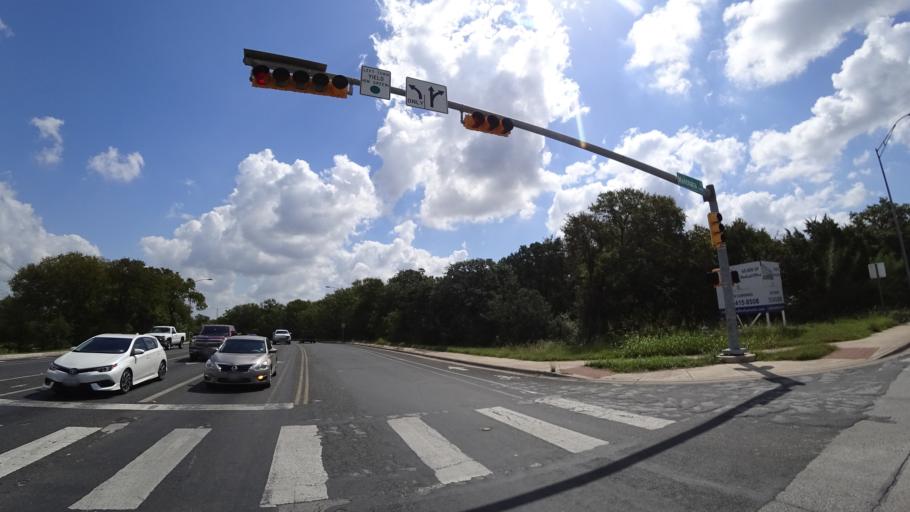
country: US
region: Texas
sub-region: Travis County
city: Manchaca
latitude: 30.1859
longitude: -97.8162
